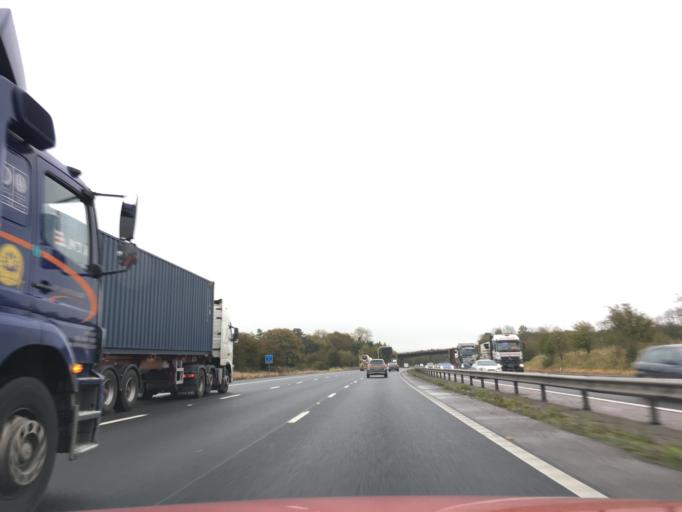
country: GB
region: England
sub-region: Borough of Swindon
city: Wanborough
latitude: 51.5269
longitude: -1.6816
